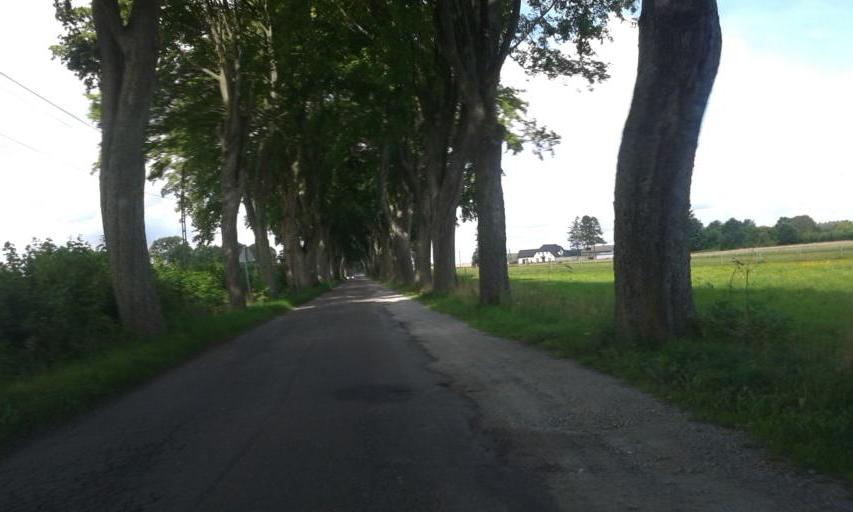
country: PL
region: West Pomeranian Voivodeship
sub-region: Powiat slawienski
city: Slawno
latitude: 54.3105
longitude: 16.6183
